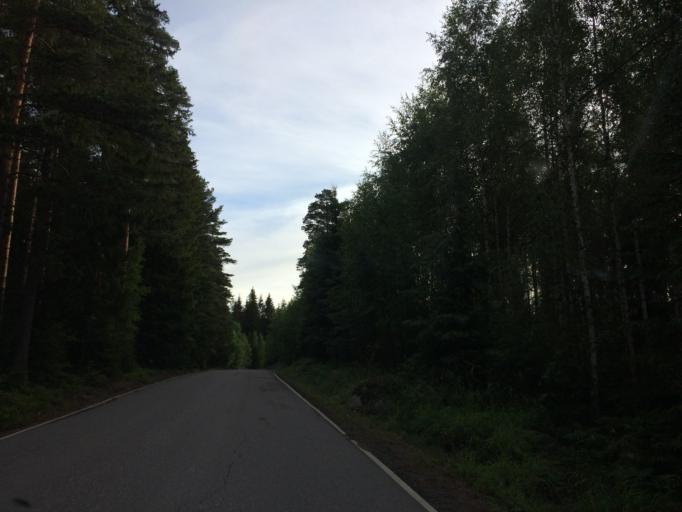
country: FI
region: Haeme
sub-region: Haemeenlinna
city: Janakkala
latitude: 60.8589
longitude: 24.5450
